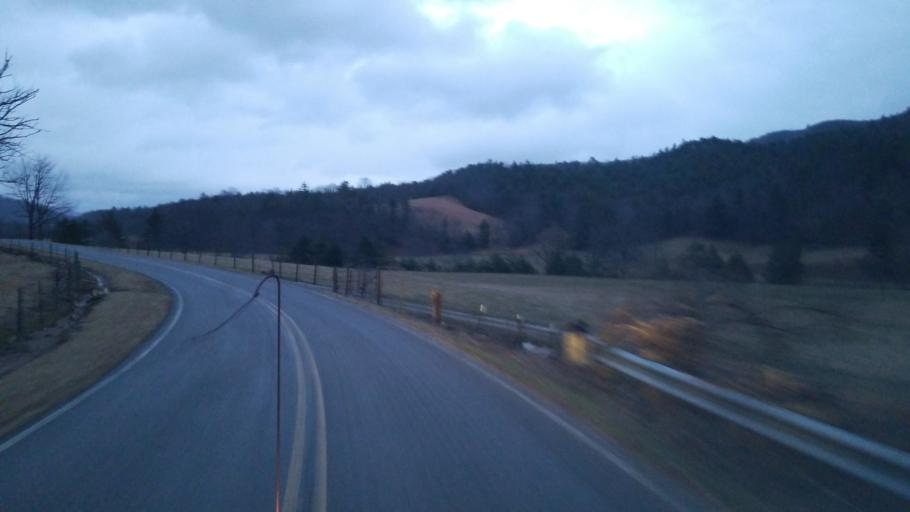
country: US
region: Virginia
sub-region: Pulaski County
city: Pulaski
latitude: 37.1323
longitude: -80.8546
